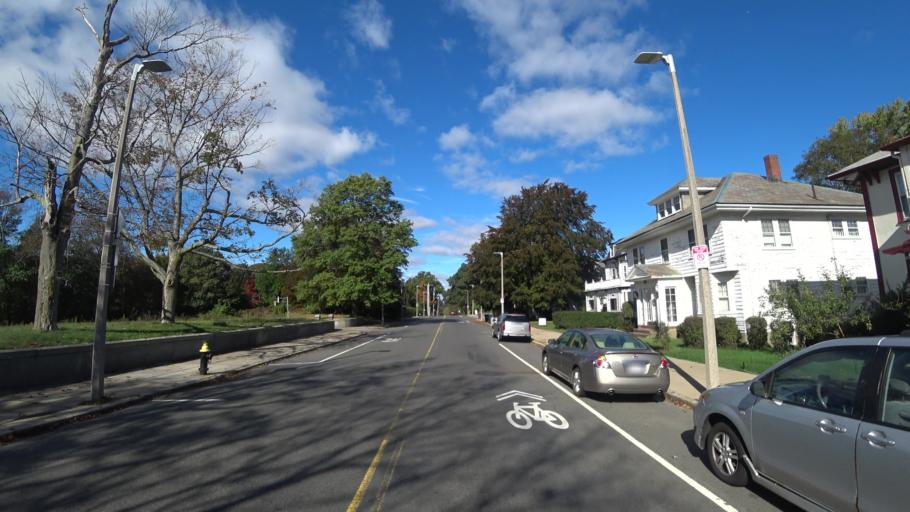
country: US
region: Massachusetts
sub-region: Middlesex County
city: Watertown
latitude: 42.3528
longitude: -71.1728
